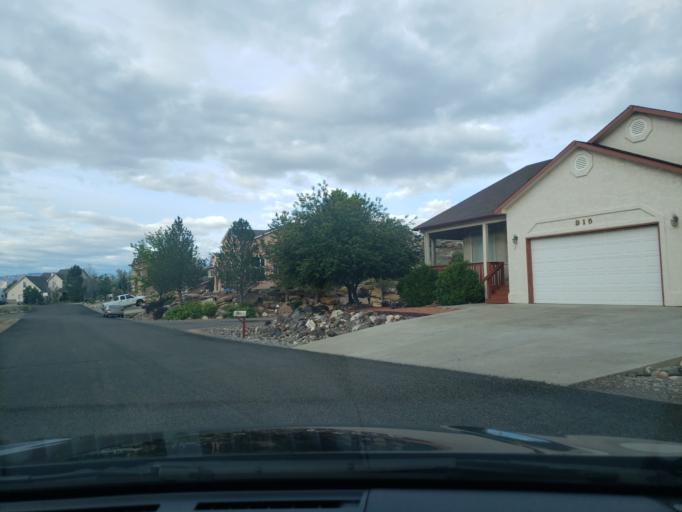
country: US
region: Colorado
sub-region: Mesa County
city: Fruita
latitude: 39.1359
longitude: -108.7439
